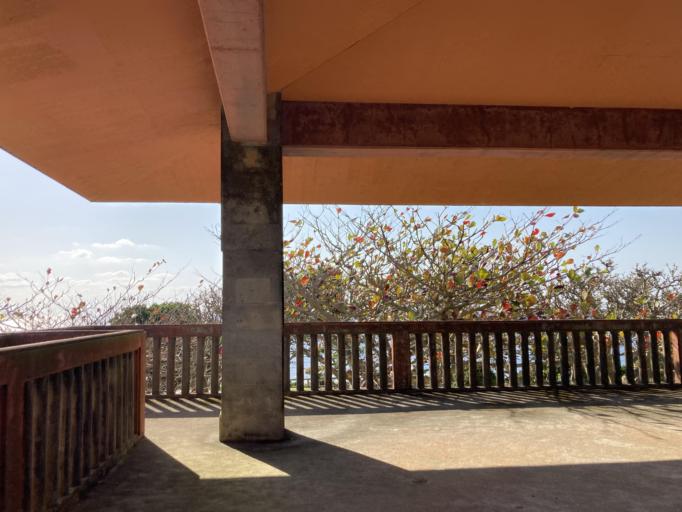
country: JP
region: Okinawa
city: Itoman
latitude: 26.1214
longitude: 127.7501
